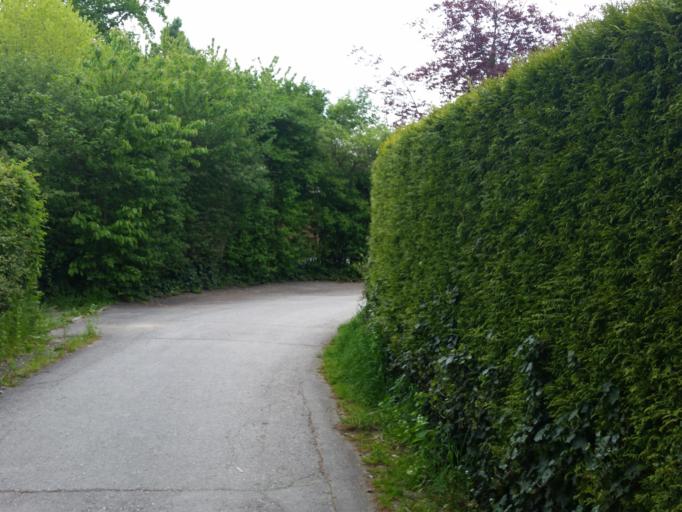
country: CH
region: Thurgau
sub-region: Kreuzlingen District
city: Altnau
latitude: 47.6205
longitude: 9.2736
